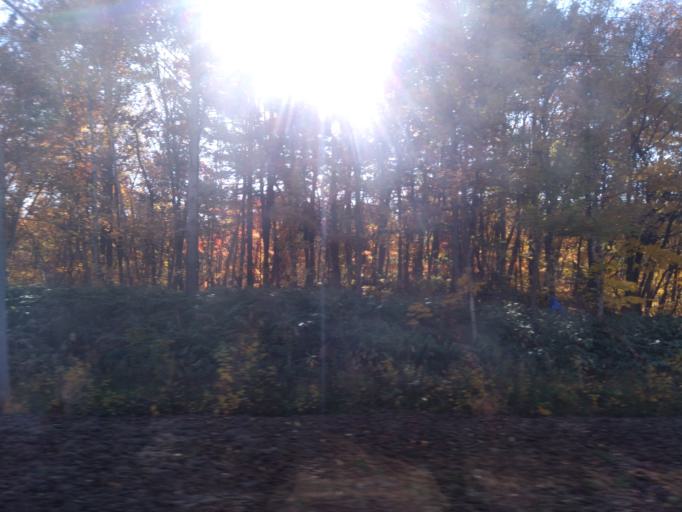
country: JP
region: Hokkaido
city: Kitahiroshima
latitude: 42.9965
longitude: 141.5359
